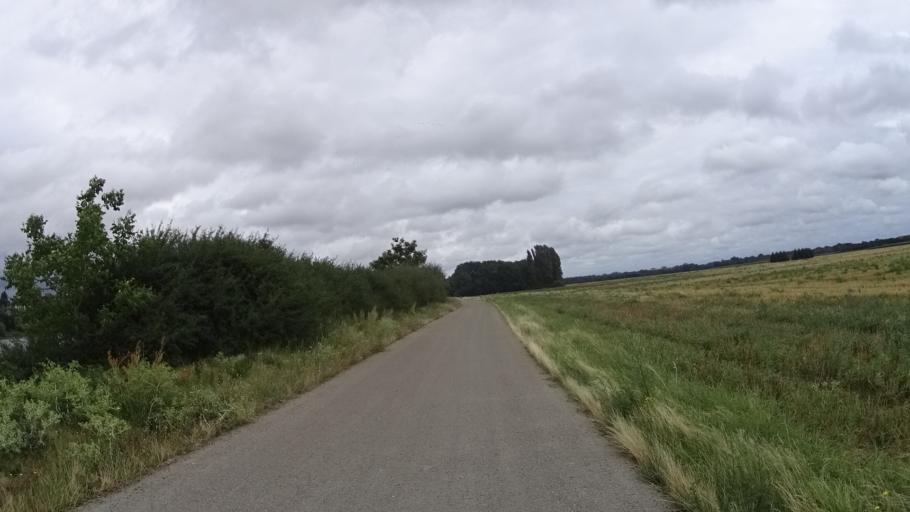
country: FR
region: Centre
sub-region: Departement du Loiret
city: Meung-sur-Loire
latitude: 47.8274
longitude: 1.7094
